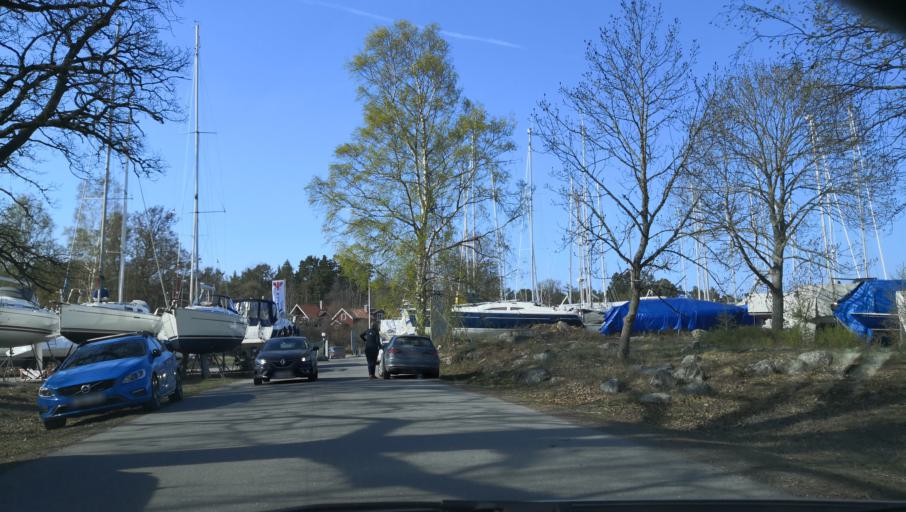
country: SE
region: Stockholm
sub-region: Varmdo Kommun
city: Holo
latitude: 59.3012
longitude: 18.6507
